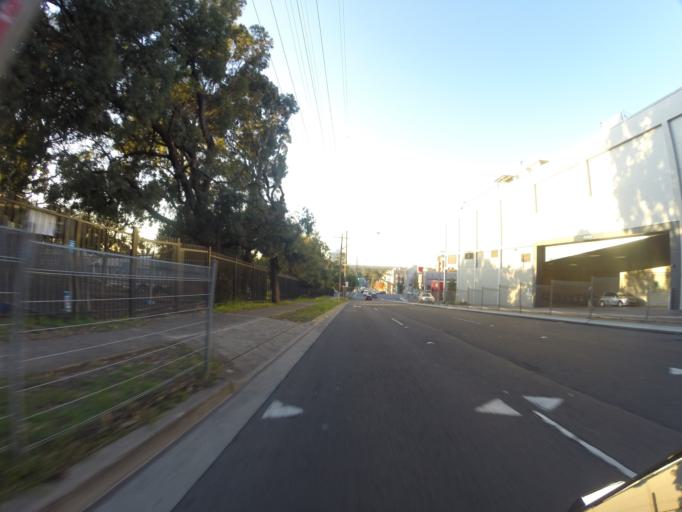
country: AU
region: New South Wales
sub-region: Sutherland Shire
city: Miranda
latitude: -34.0349
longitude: 151.0984
